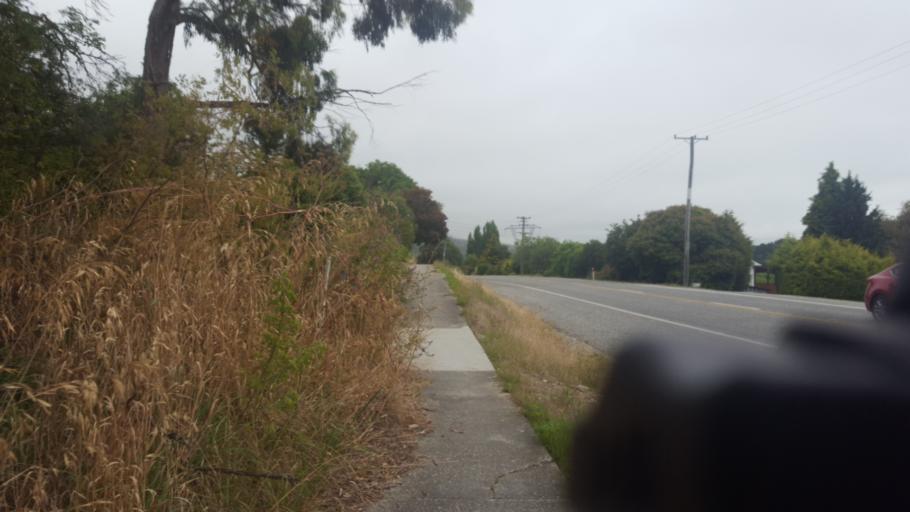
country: NZ
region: Otago
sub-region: Queenstown-Lakes District
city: Kingston
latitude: -45.5312
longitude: 169.2989
